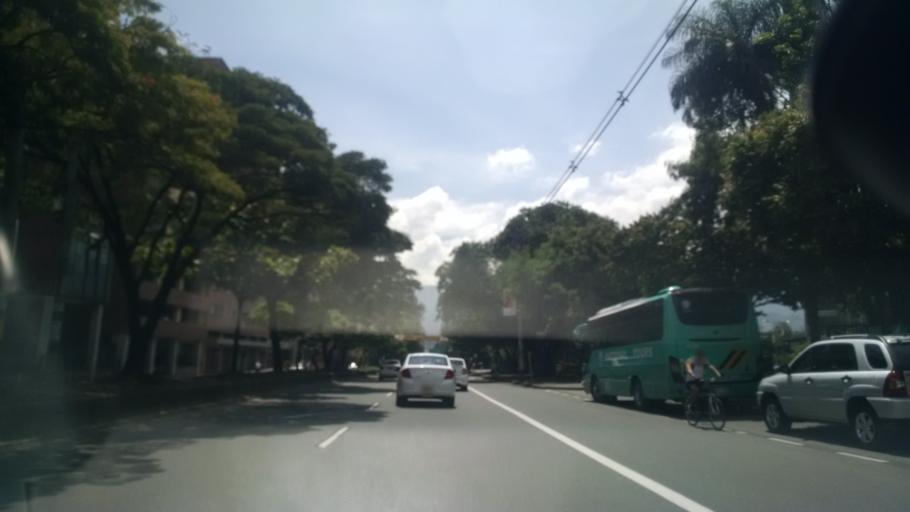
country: CO
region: Antioquia
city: Medellin
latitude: 6.2599
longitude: -75.5891
